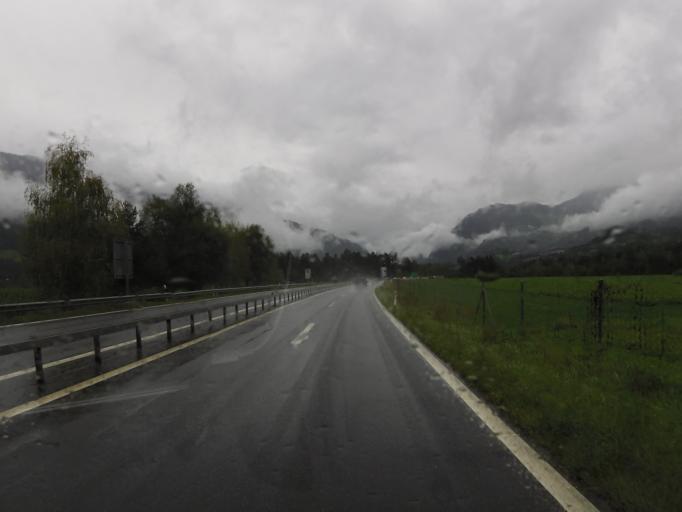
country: CH
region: Grisons
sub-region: Hinterrhein District
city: Cazis
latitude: 46.7189
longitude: 9.4414
